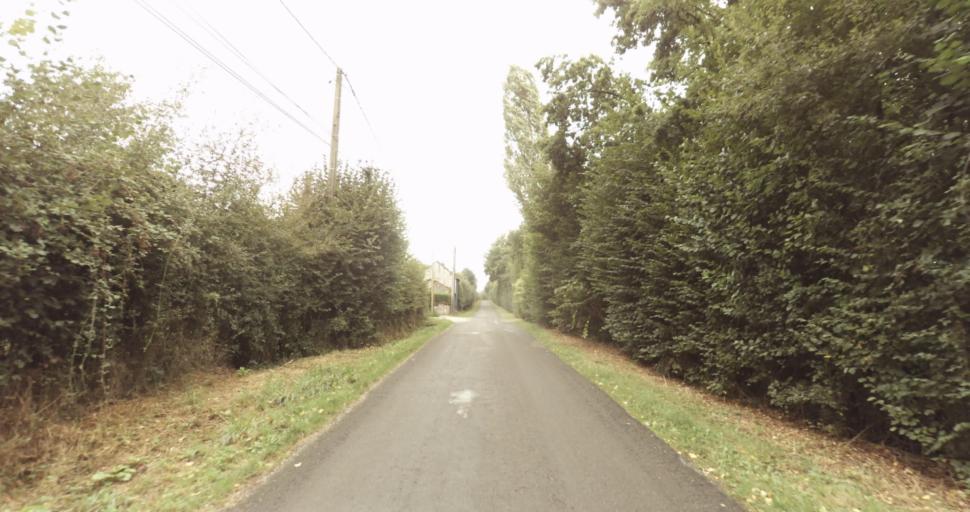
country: FR
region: Lower Normandy
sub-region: Departement de l'Orne
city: Sainte-Gauburge-Sainte-Colombe
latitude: 48.7036
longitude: 0.4487
